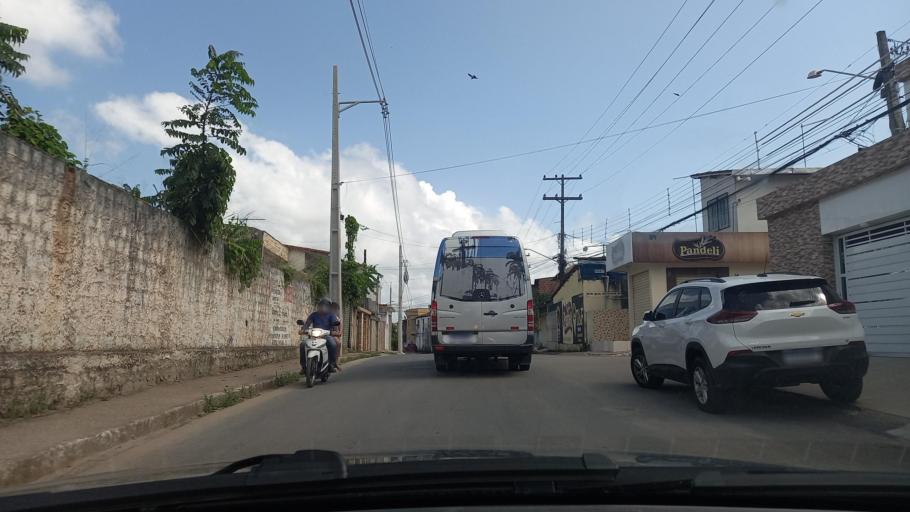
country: BR
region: Pernambuco
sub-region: Goiana
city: Goiana
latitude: -7.5653
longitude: -35.0016
